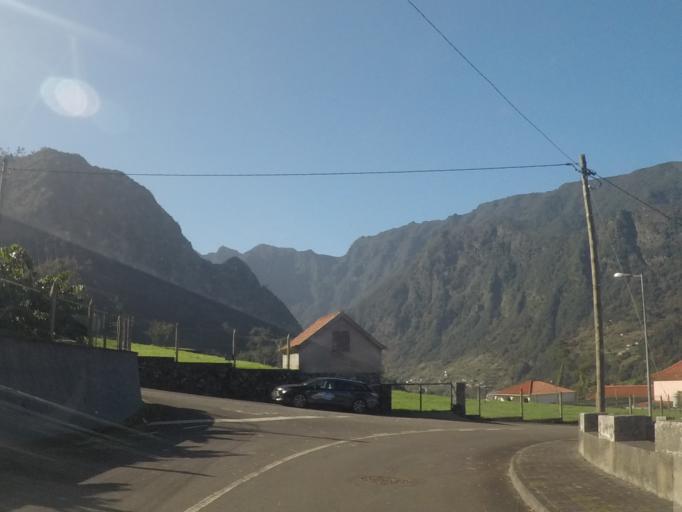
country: PT
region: Madeira
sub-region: Santana
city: Santana
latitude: 32.8008
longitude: -16.9599
